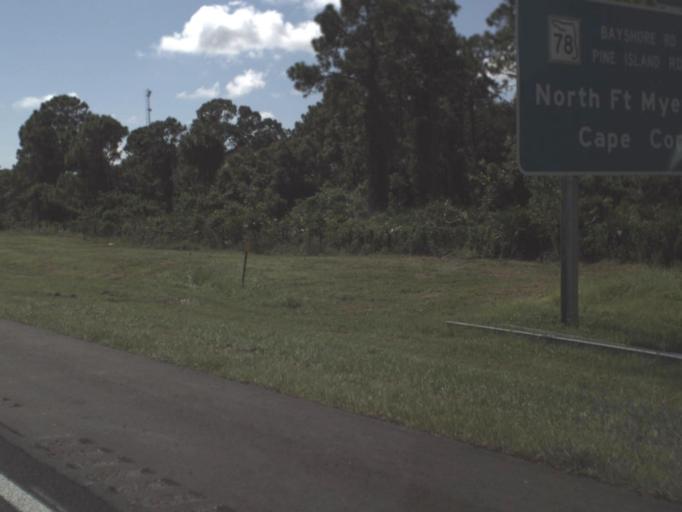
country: US
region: Florida
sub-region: Lee County
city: Tice
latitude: 26.7201
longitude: -81.8167
